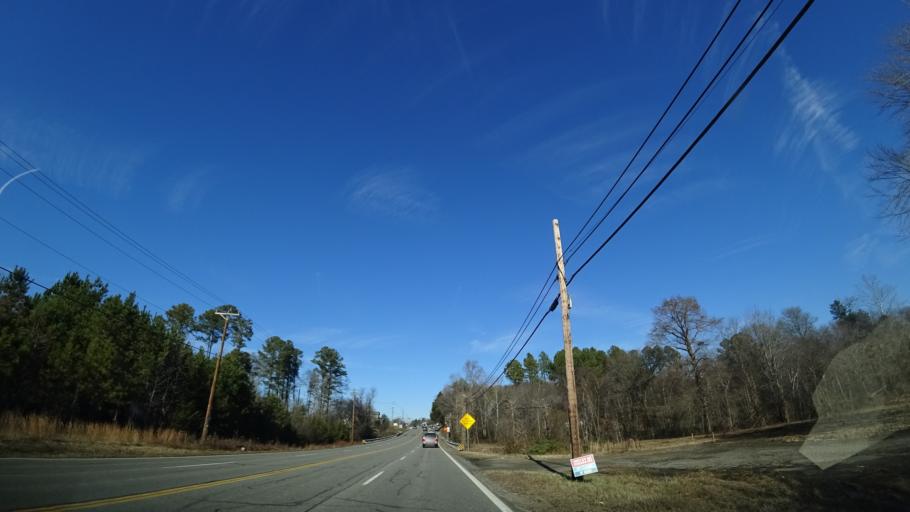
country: US
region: Virginia
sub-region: Henrico County
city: Glen Allen
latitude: 37.6944
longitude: -77.4631
